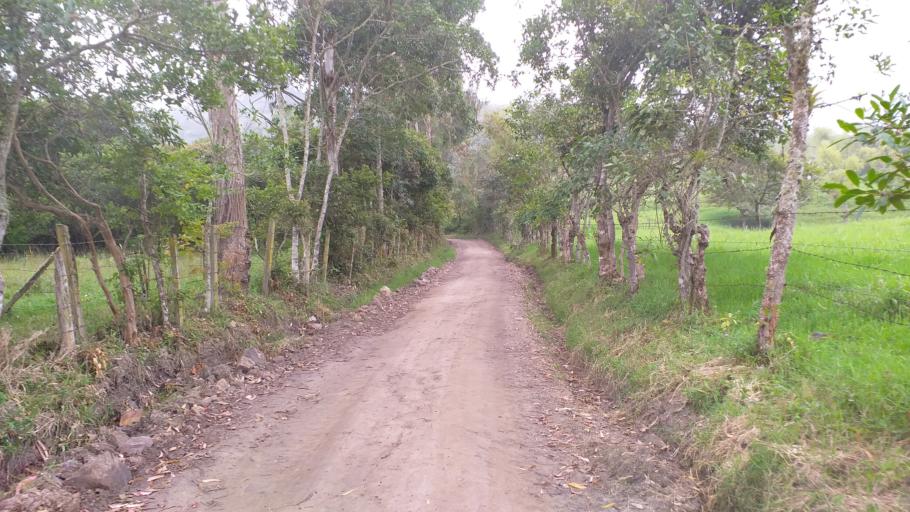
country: CO
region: Cundinamarca
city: Tenza
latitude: 5.0899
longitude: -73.4535
